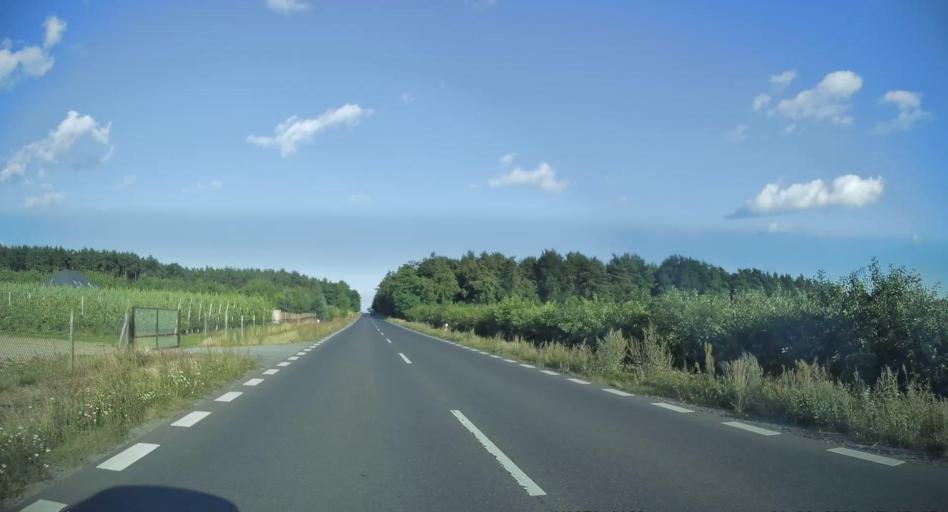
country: PL
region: Lodz Voivodeship
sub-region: Powiat rawski
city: Biala Rawska
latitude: 51.8018
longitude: 20.5096
